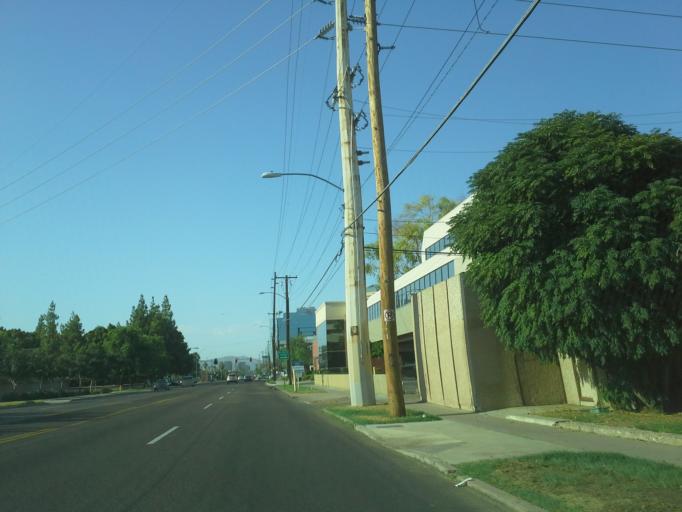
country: US
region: Arizona
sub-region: Maricopa County
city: Phoenix
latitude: 33.4894
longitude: -112.0695
